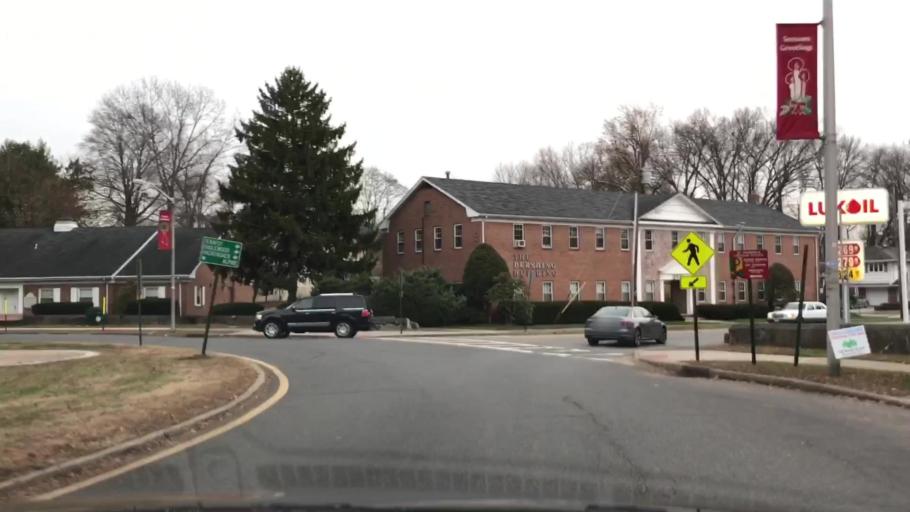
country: US
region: New Jersey
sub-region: Bergen County
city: Cresskill
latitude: 40.9411
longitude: -73.9772
